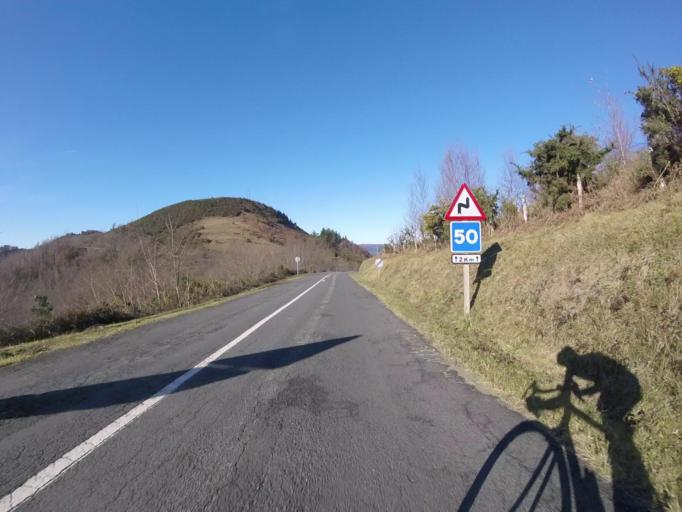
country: ES
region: Basque Country
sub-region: Provincia de Guipuzcoa
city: Irun
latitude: 43.2927
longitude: -1.8108
